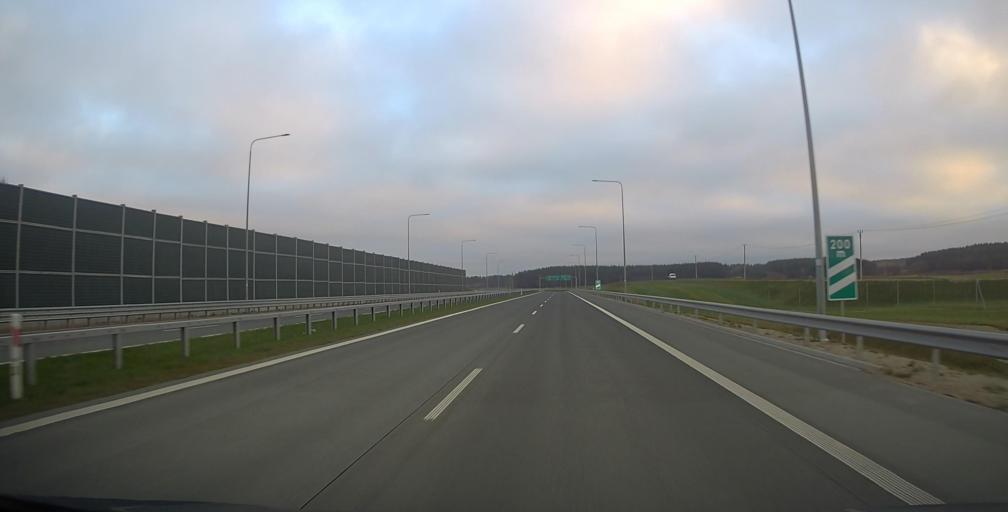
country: PL
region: Podlasie
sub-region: Powiat kolnenski
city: Stawiski
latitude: 53.4528
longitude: 22.1914
